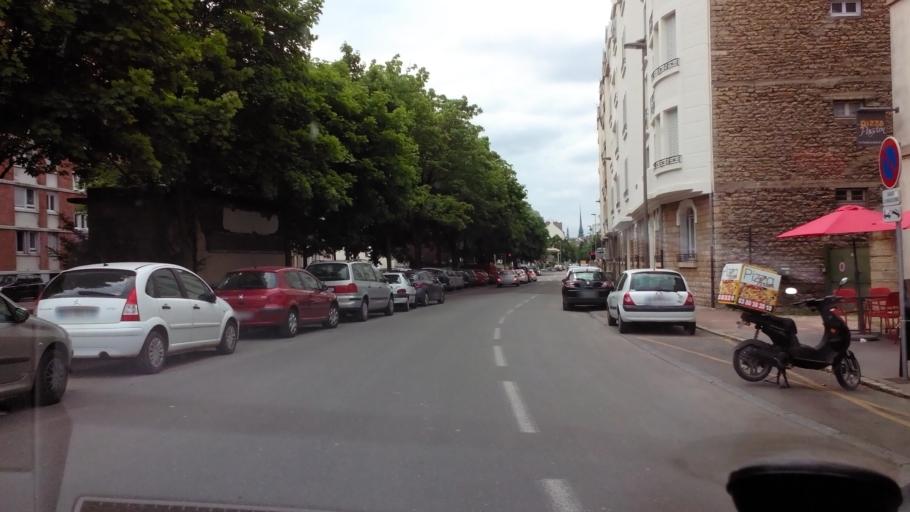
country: FR
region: Bourgogne
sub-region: Departement de la Cote-d'Or
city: Fontaine-les-Dijon
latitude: 47.3291
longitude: 5.0430
